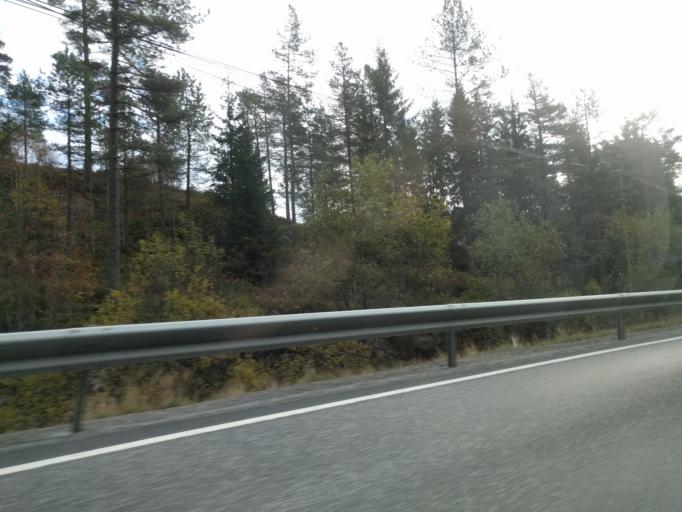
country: NO
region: Vest-Agder
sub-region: Songdalen
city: Nodeland
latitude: 58.3029
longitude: 7.8185
